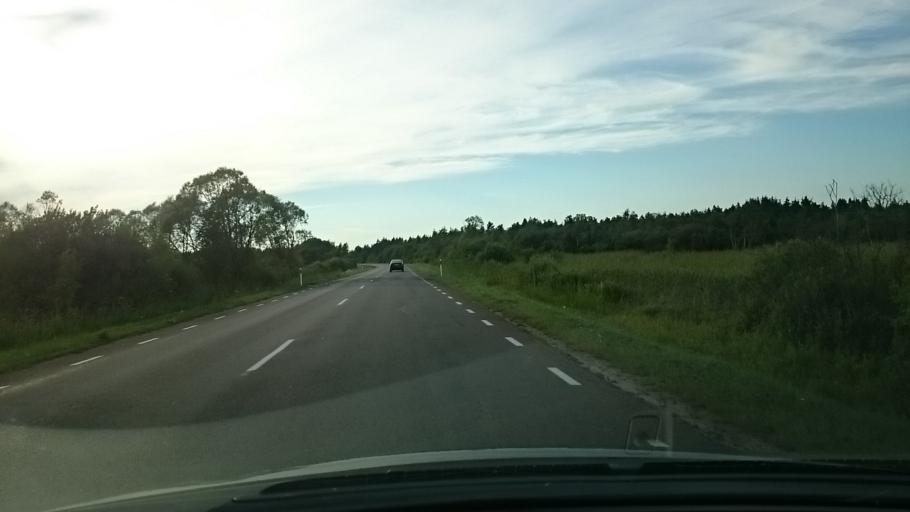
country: EE
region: Saare
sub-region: Kuressaare linn
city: Kuressaare
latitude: 58.2832
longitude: 22.4239
